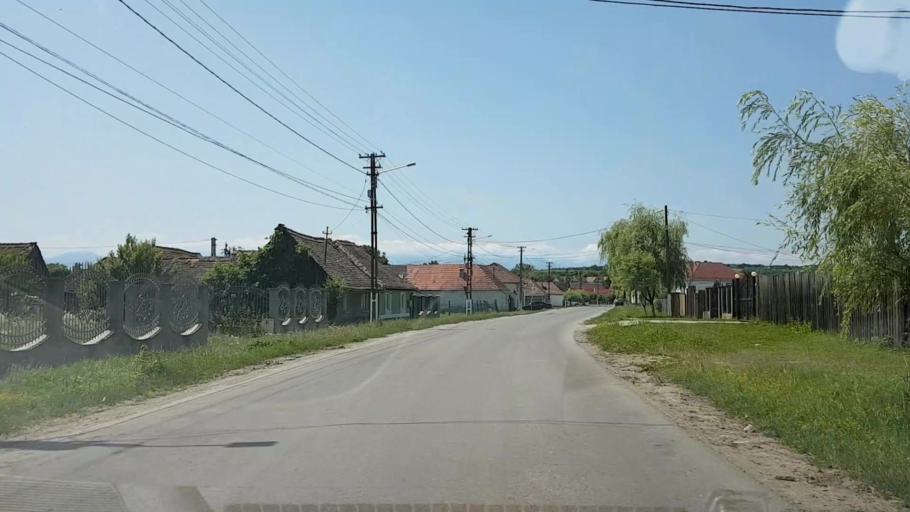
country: RO
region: Brasov
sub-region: Comuna Cincu
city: Cincu
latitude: 45.9159
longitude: 24.8087
